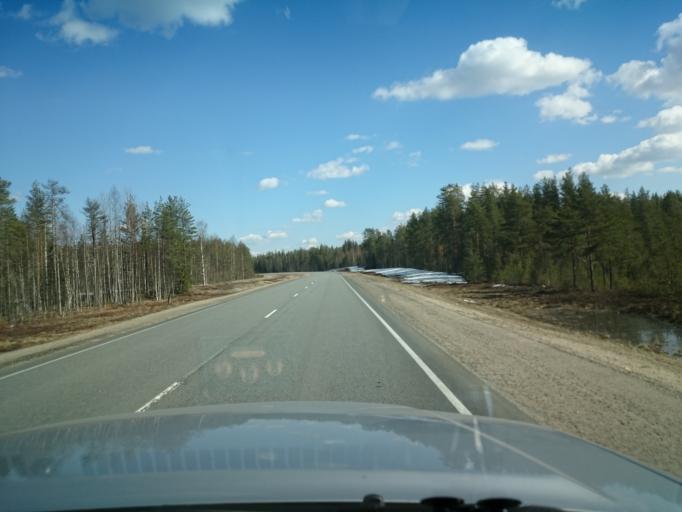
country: RU
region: Republic of Karelia
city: Pryazha
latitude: 61.4593
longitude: 33.3140
